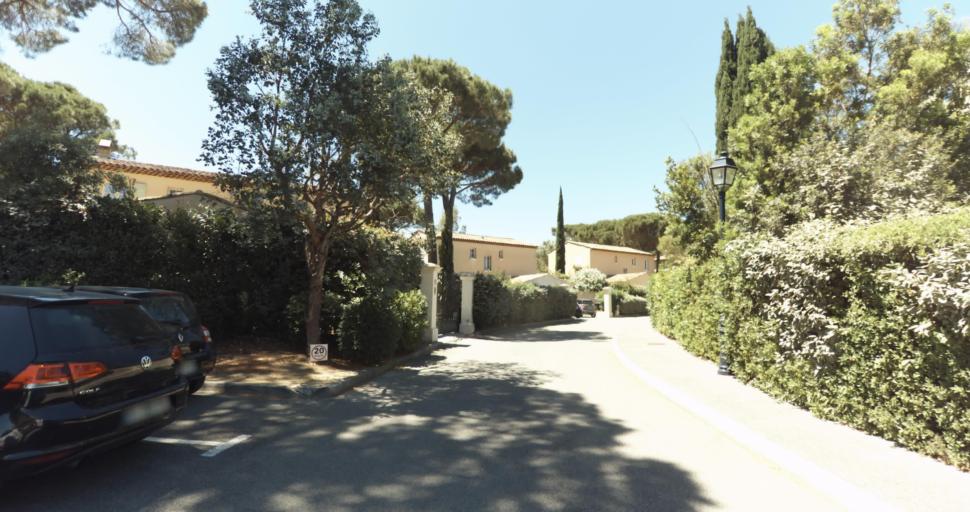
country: FR
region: Provence-Alpes-Cote d'Azur
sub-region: Departement du Var
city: Gassin
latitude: 43.2524
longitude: 6.5718
